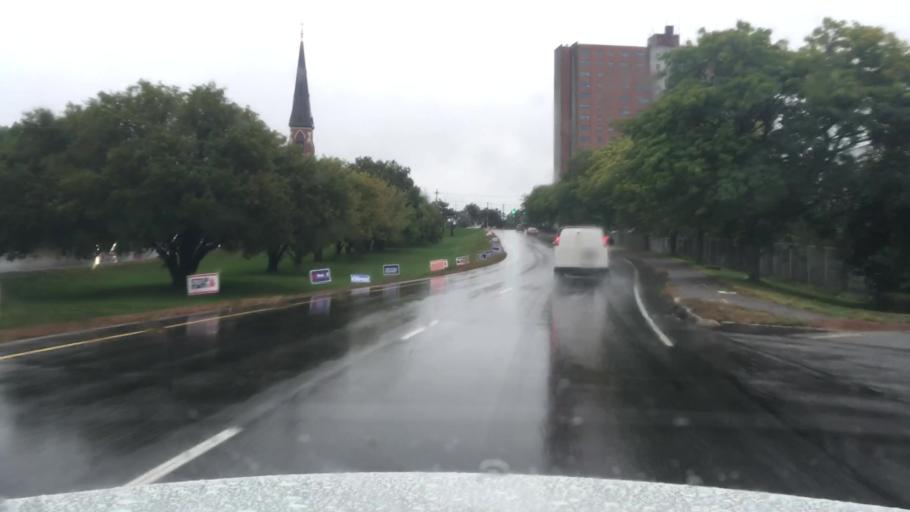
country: US
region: Maine
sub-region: Cumberland County
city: Portland
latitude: 43.6619
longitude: -70.2547
